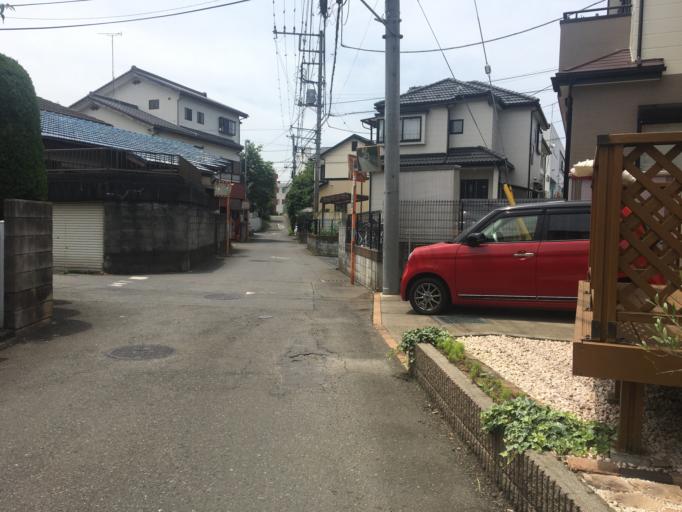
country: JP
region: Saitama
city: Sayama
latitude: 35.8426
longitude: 139.4245
